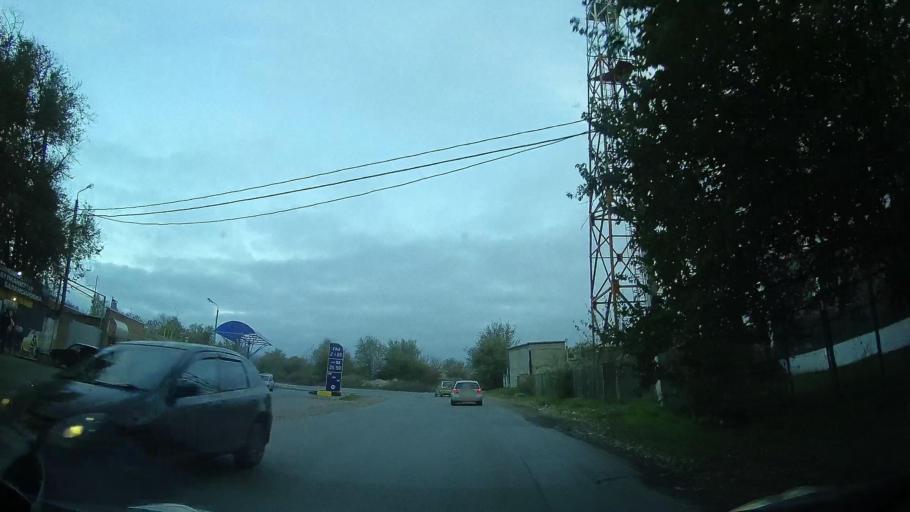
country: RU
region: Rostov
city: Severnyy
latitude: 47.2651
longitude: 39.6482
